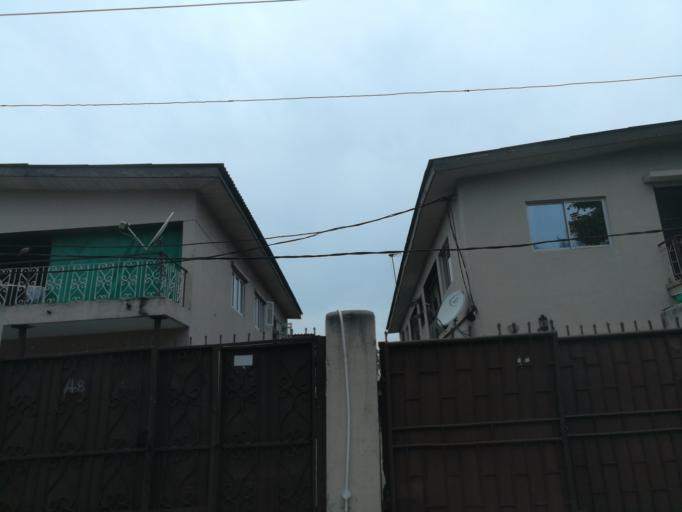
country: NG
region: Lagos
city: Makoko
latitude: 6.5032
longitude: 3.3888
